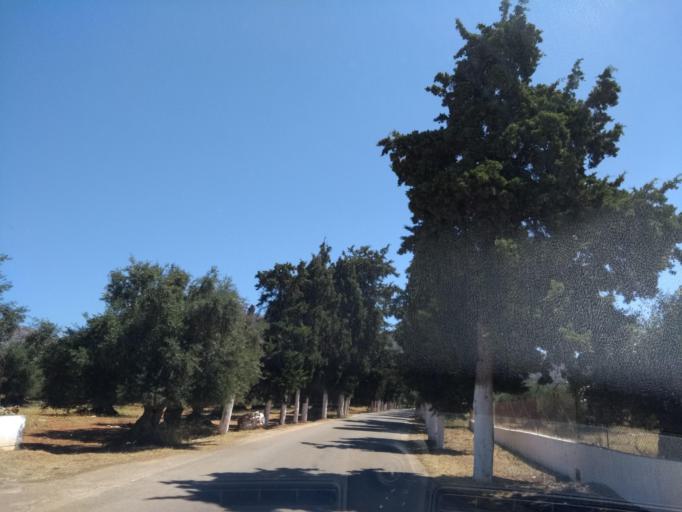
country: GR
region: Crete
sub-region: Nomos Chanias
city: Mouzouras
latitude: 35.5579
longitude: 24.1284
